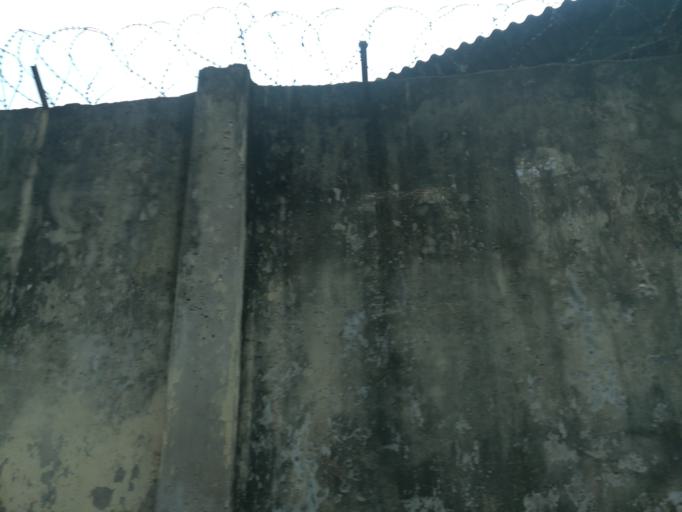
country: NG
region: Lagos
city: Oshodi
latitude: 6.5700
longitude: 3.3419
